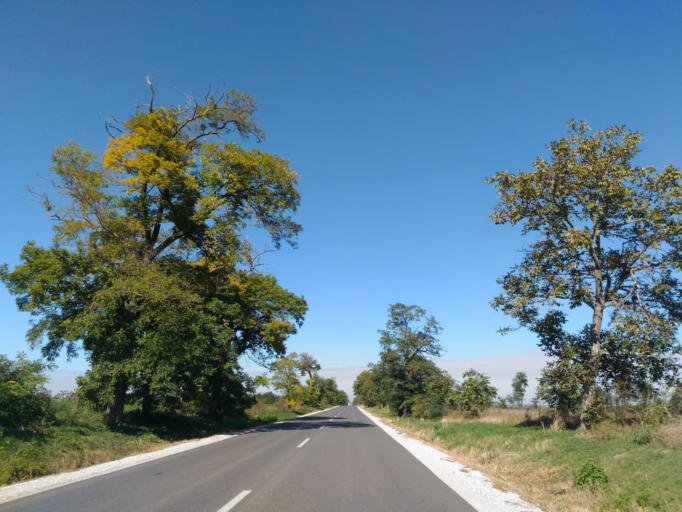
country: HU
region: Fejer
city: Kapolnasnyek
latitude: 47.1919
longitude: 18.7050
